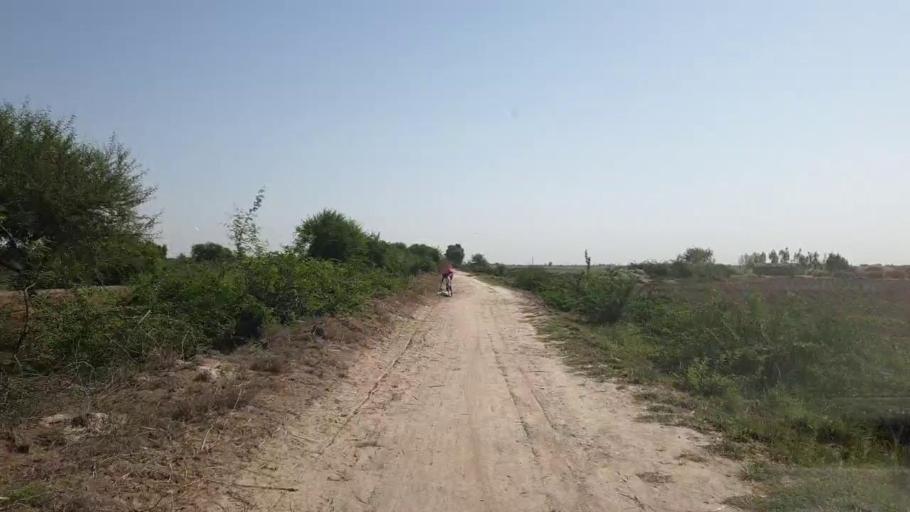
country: PK
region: Sindh
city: Kadhan
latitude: 24.6115
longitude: 68.9991
